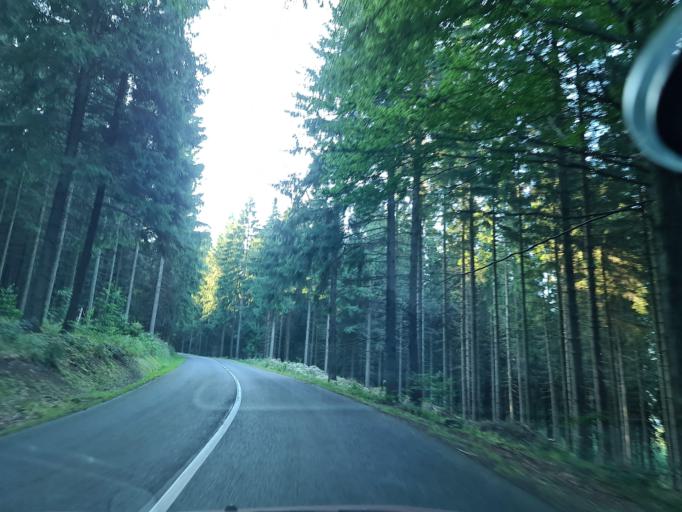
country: DE
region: Saxony
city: Seiffen
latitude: 50.6211
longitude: 13.4114
